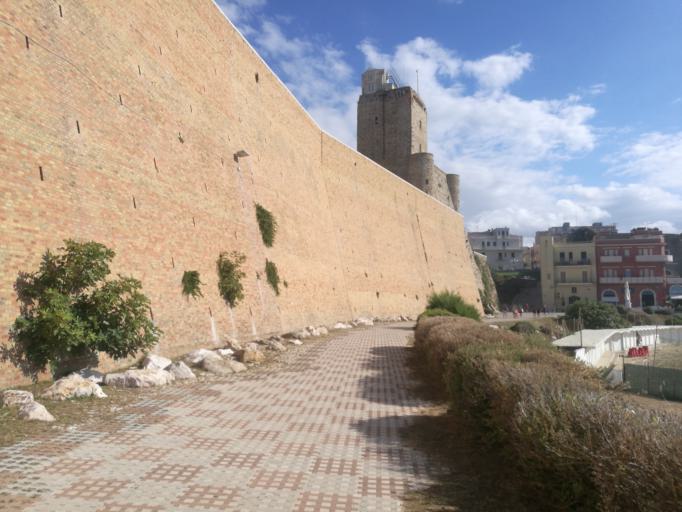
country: IT
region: Molise
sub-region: Provincia di Campobasso
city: Termoli
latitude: 42.0051
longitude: 14.9964
